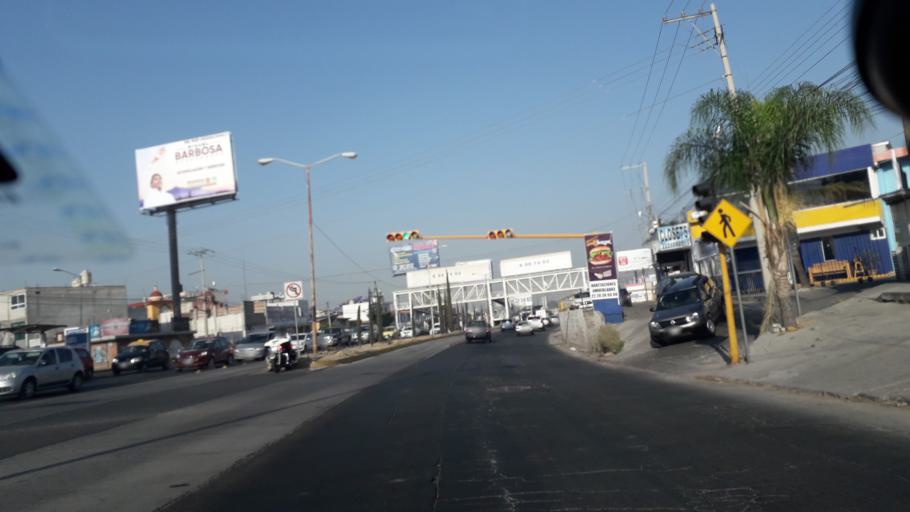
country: MX
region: Puebla
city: Tlazcalancingo
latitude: 19.0366
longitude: -98.2497
